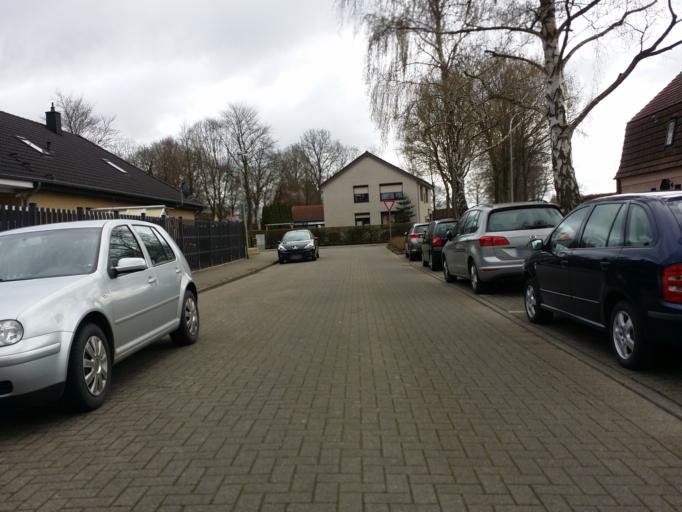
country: DE
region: Lower Saxony
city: Delmenhorst
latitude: 53.0250
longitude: 8.6333
